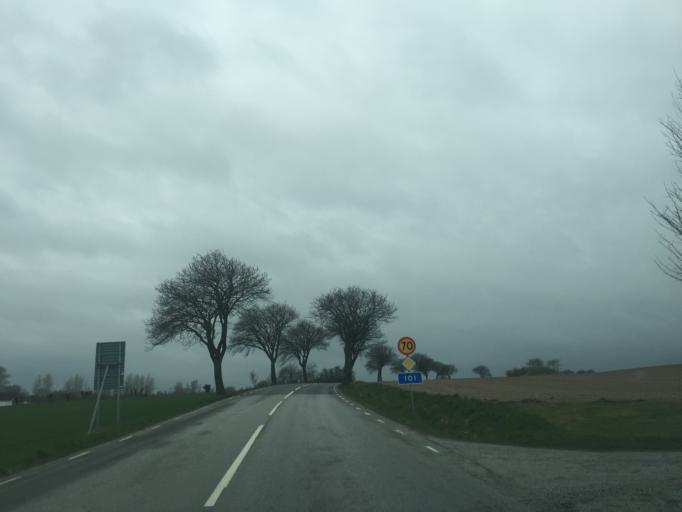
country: SE
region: Skane
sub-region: Skurups Kommun
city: Skivarp
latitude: 55.4182
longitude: 13.6357
